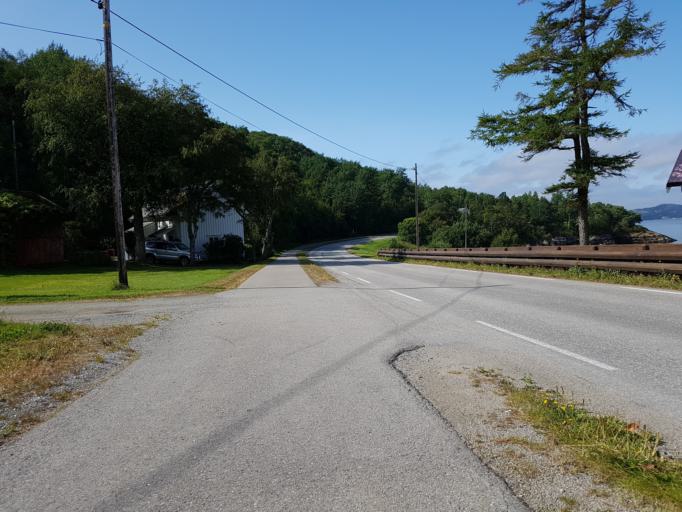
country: NO
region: Sor-Trondelag
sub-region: Agdenes
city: Lensvik
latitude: 63.6354
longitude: 9.8385
